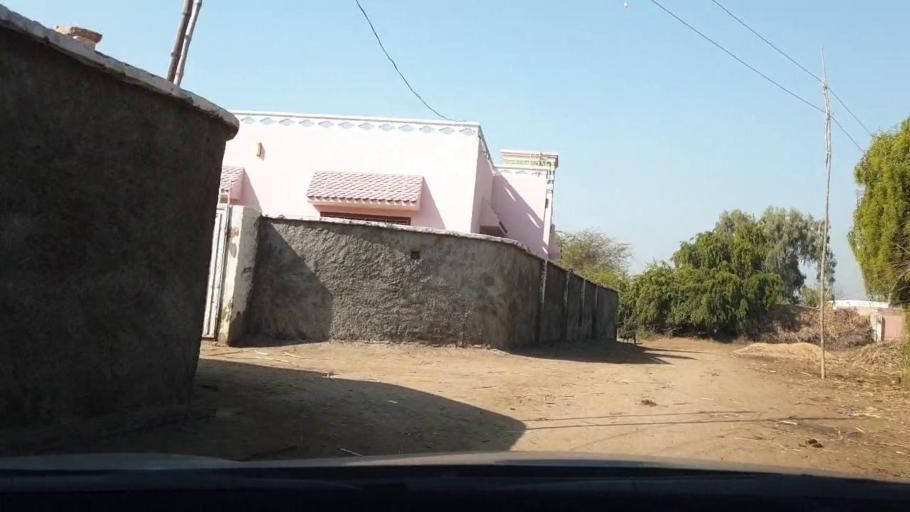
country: PK
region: Sindh
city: Tando Allahyar
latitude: 25.5059
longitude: 68.6918
